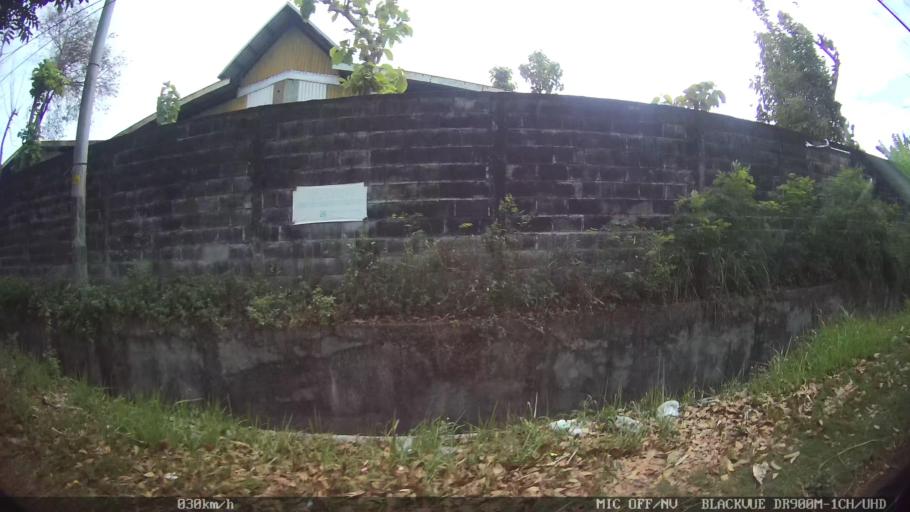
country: ID
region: Daerah Istimewa Yogyakarta
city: Depok
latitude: -7.8048
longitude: 110.4472
